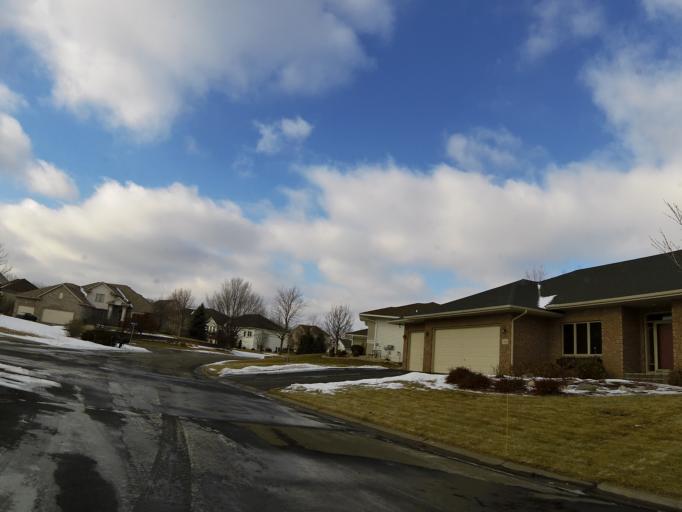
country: US
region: Minnesota
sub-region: Scott County
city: Prior Lake
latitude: 44.7298
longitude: -93.4511
